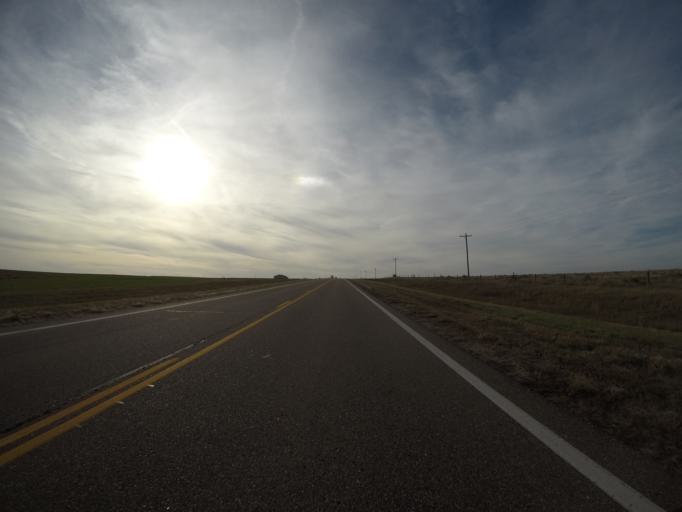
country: US
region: Kansas
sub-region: Cheyenne County
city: Saint Francis
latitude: 39.7566
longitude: -101.7608
